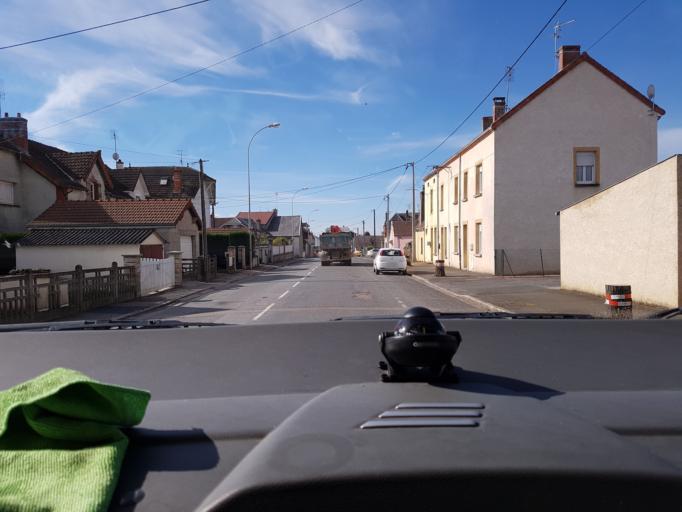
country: FR
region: Bourgogne
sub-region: Departement de Saone-et-Loire
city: Gueugnon
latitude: 46.6002
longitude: 4.0692
